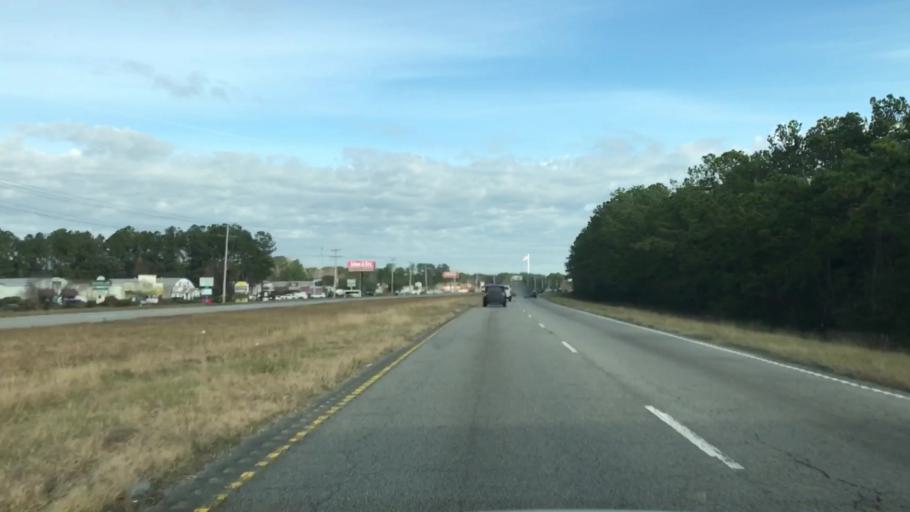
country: US
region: South Carolina
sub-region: Horry County
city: Garden City
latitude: 33.5912
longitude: -79.0257
